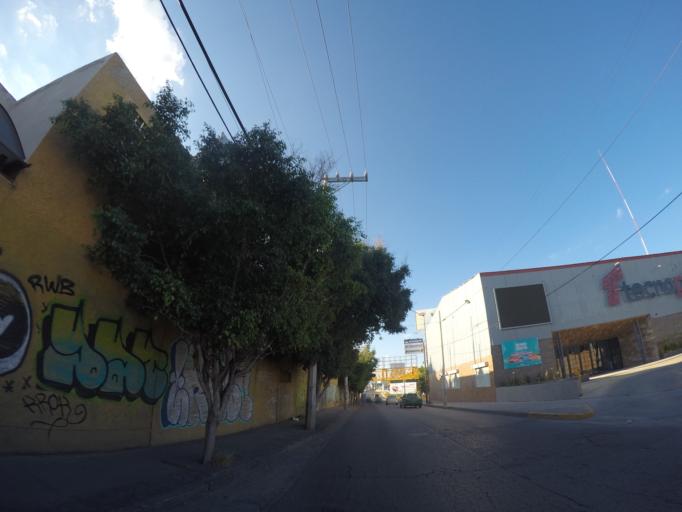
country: MX
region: San Luis Potosi
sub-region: San Luis Potosi
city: San Luis Potosi
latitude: 22.1570
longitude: -100.9999
